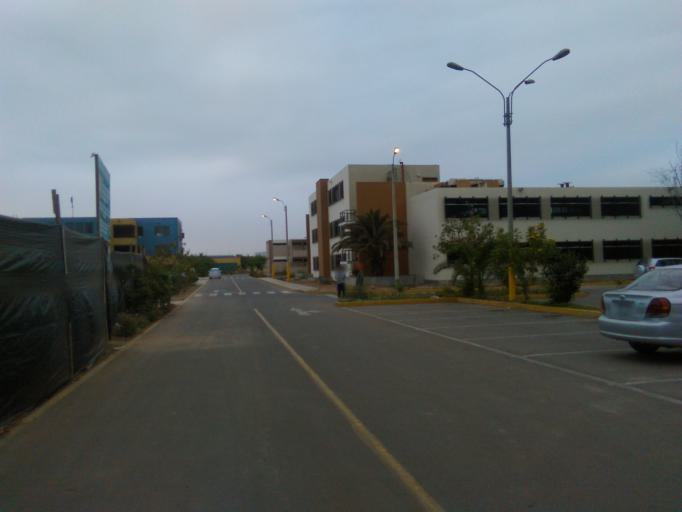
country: PE
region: Callao
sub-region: Callao
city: Callao
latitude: -12.0562
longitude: -77.0868
